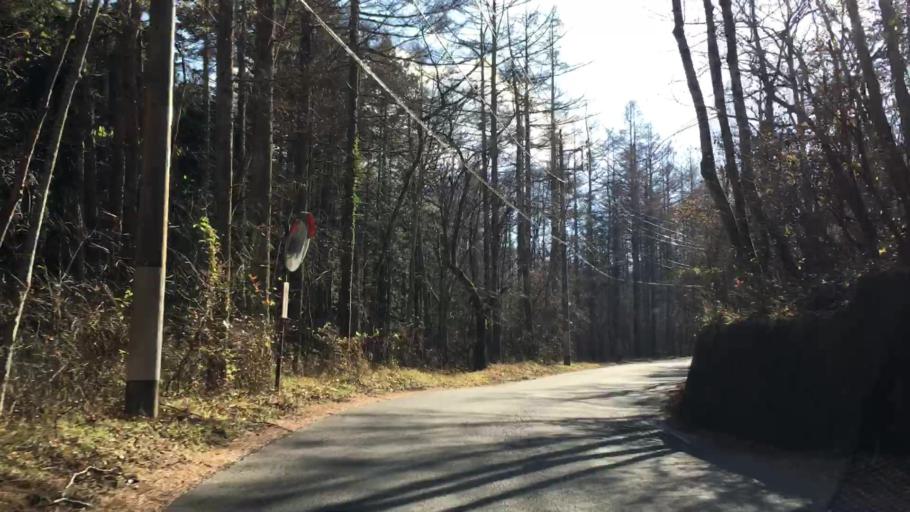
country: JP
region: Shizuoka
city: Gotemba
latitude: 35.4022
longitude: 138.8648
